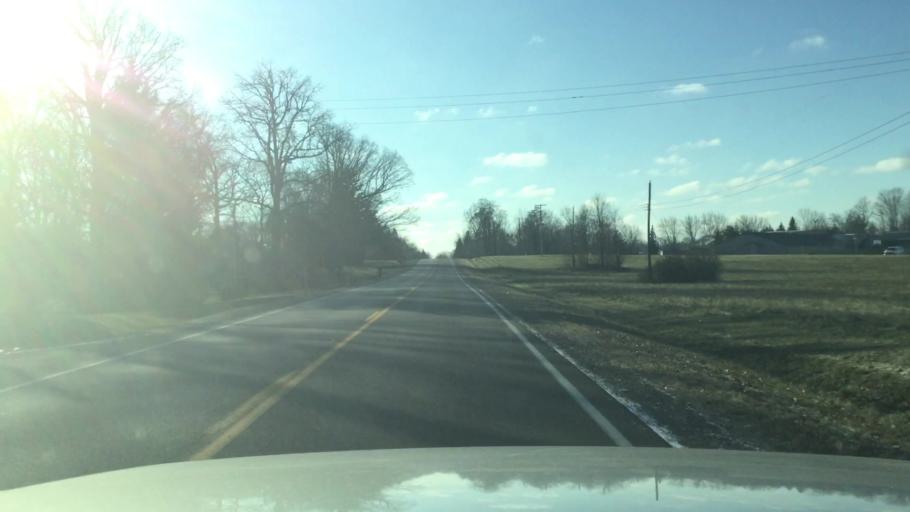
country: US
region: Michigan
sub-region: Genesee County
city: Grand Blanc
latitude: 42.9331
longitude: -83.6621
